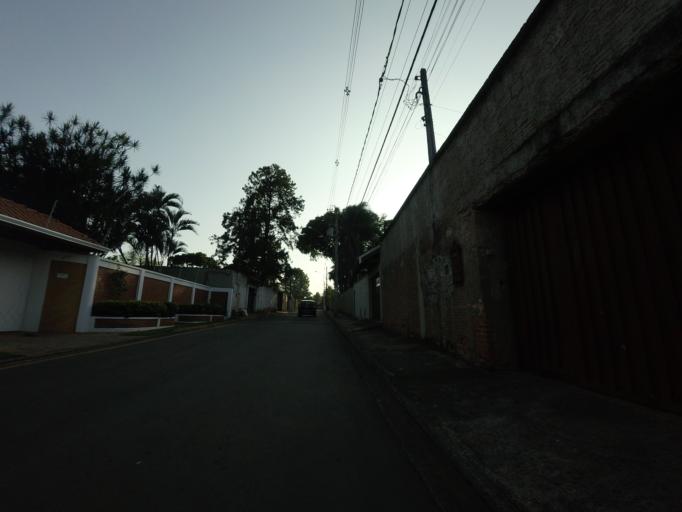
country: BR
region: Sao Paulo
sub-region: Piracicaba
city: Piracicaba
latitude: -22.7431
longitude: -47.6050
